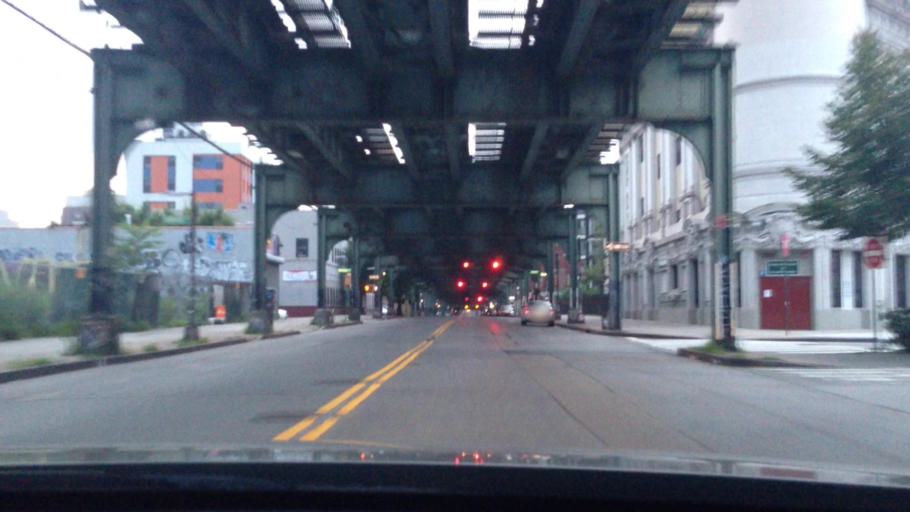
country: US
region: New York
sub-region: Kings County
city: East New York
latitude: 40.6891
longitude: -73.9213
